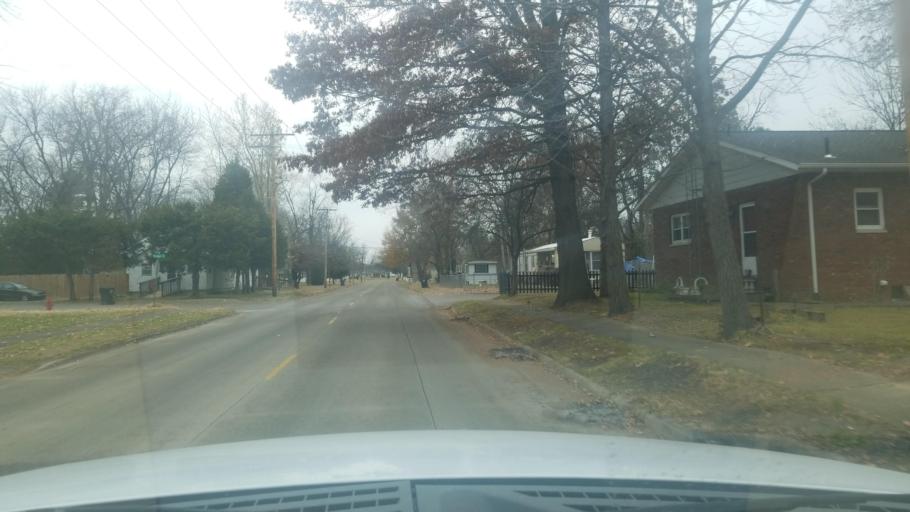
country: US
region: Illinois
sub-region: Saline County
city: Harrisburg
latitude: 37.7329
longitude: -88.5529
